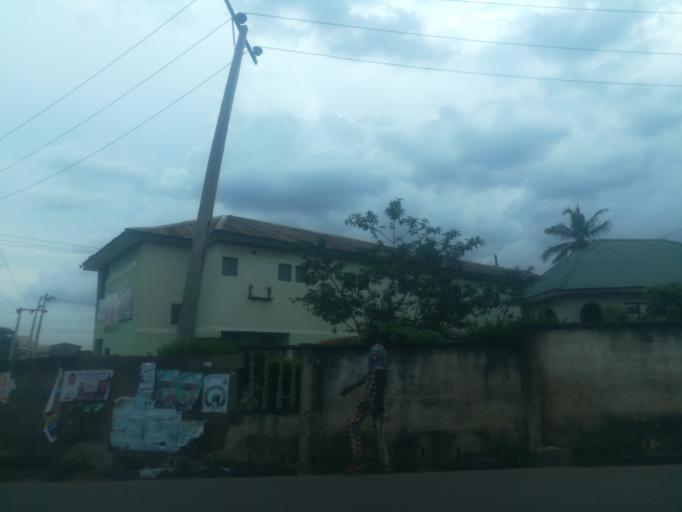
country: NG
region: Oyo
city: Ibadan
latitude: 7.4268
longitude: 3.8835
